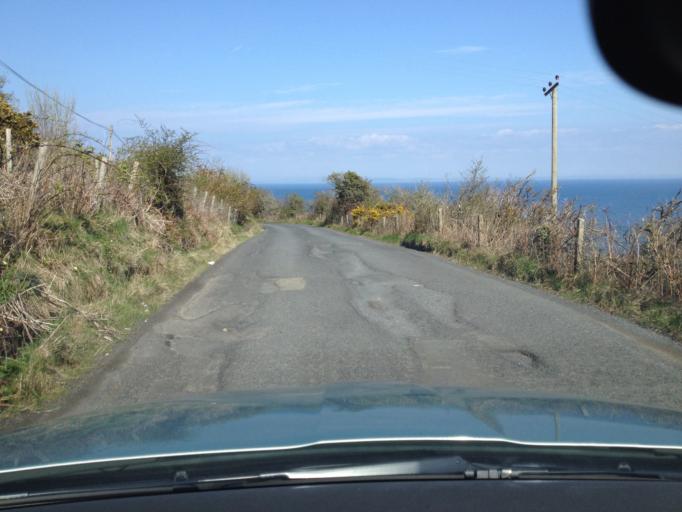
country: GB
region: Scotland
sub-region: North Ayrshire
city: Lamlash
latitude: 55.4635
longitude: -5.0869
